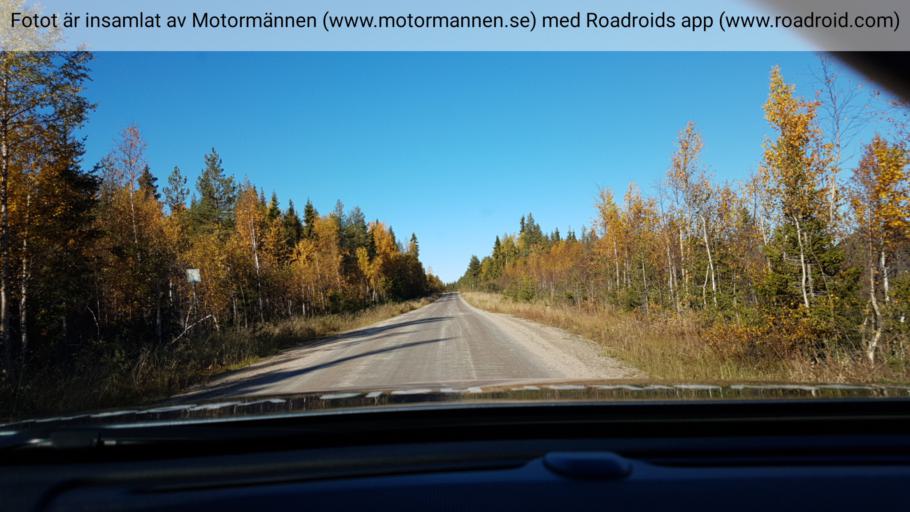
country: SE
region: Norrbotten
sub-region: Gallivare Kommun
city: Gaellivare
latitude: 66.6583
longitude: 20.9620
